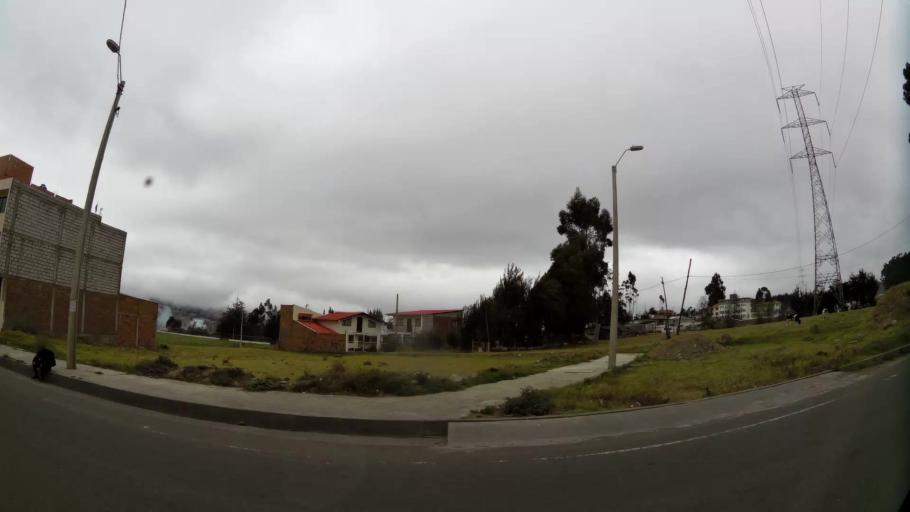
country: EC
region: Canar
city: Canar
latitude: -2.5192
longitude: -78.9272
